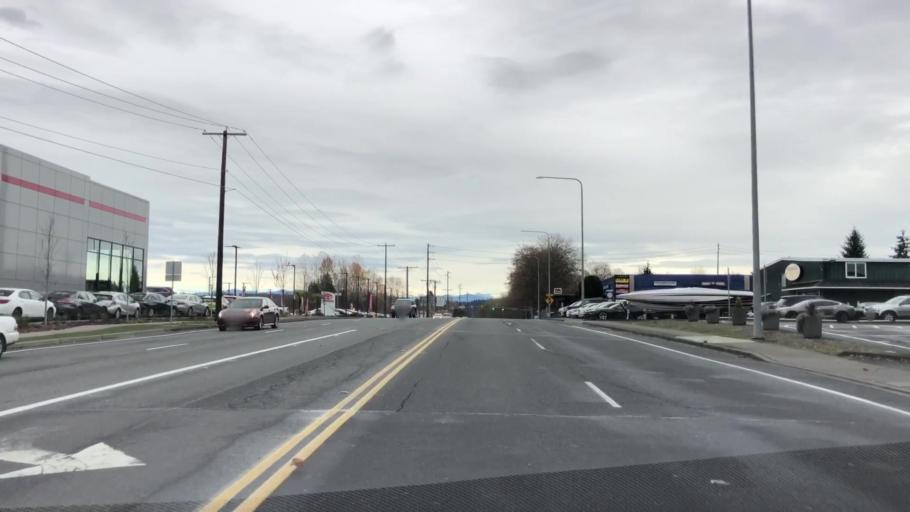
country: US
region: Washington
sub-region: King County
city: Kingsgate
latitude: 47.7115
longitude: -122.1655
